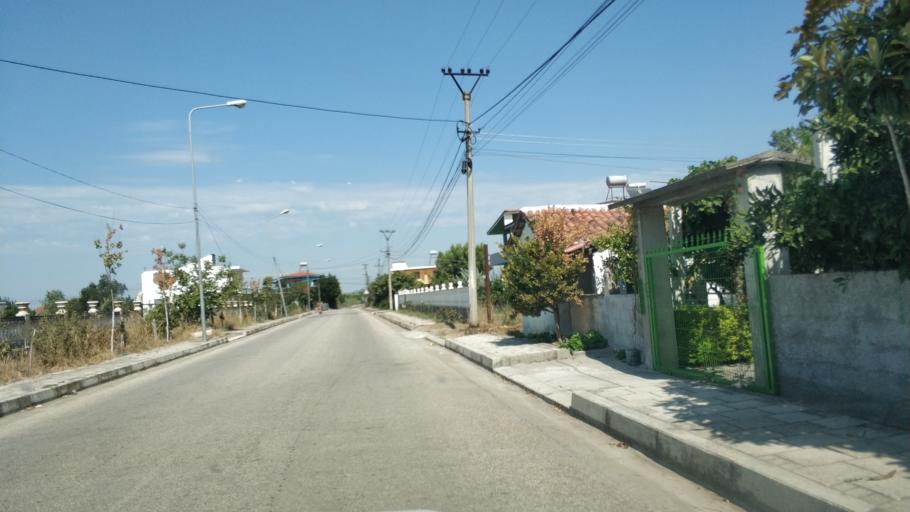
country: AL
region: Fier
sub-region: Rrethi i Lushnjes
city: Divjake
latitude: 41.0014
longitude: 19.5247
